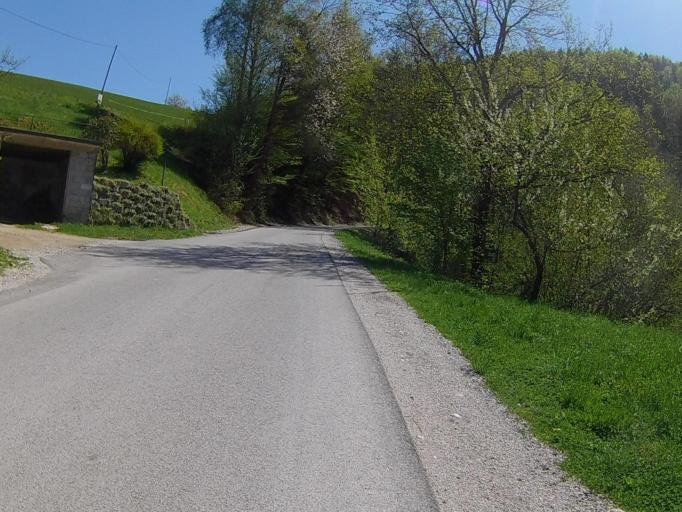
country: SI
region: Ruse
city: Ruse
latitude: 46.5275
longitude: 15.5101
